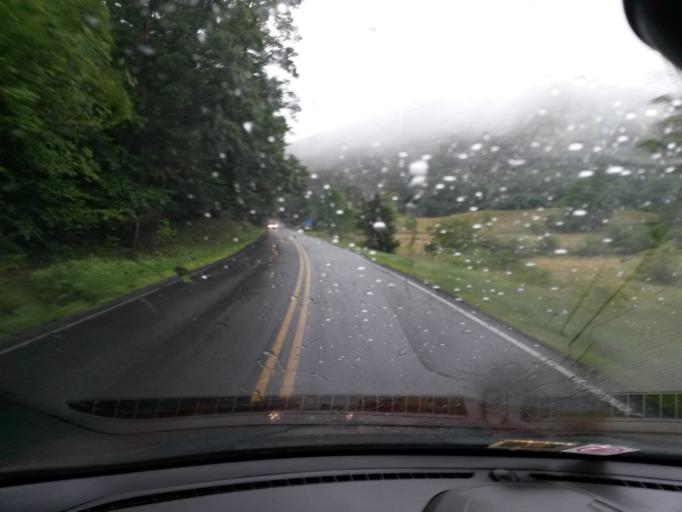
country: US
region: Virginia
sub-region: Bath County
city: Warm Springs
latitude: 38.0707
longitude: -79.7730
